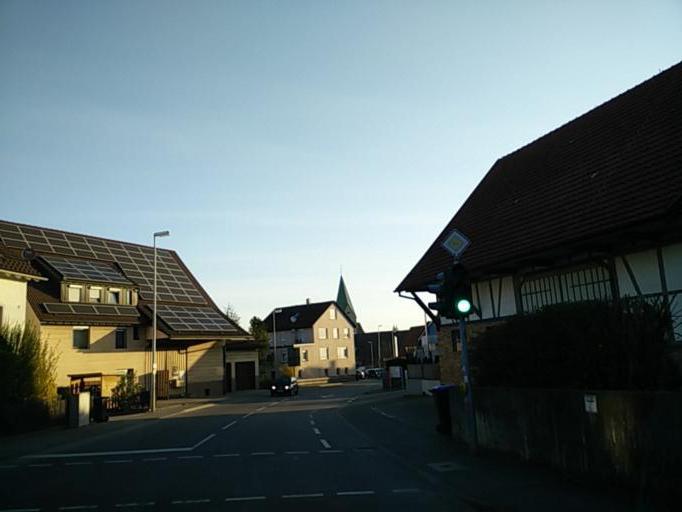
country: DE
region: Baden-Wuerttemberg
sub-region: Regierungsbezirk Stuttgart
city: Hildrizhausen
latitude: 48.6232
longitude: 8.9654
